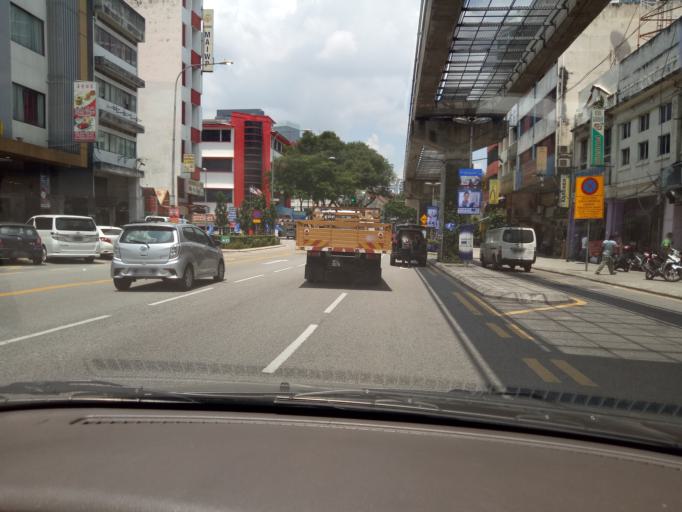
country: MY
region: Kuala Lumpur
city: Kuala Lumpur
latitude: 3.1636
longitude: 101.6981
